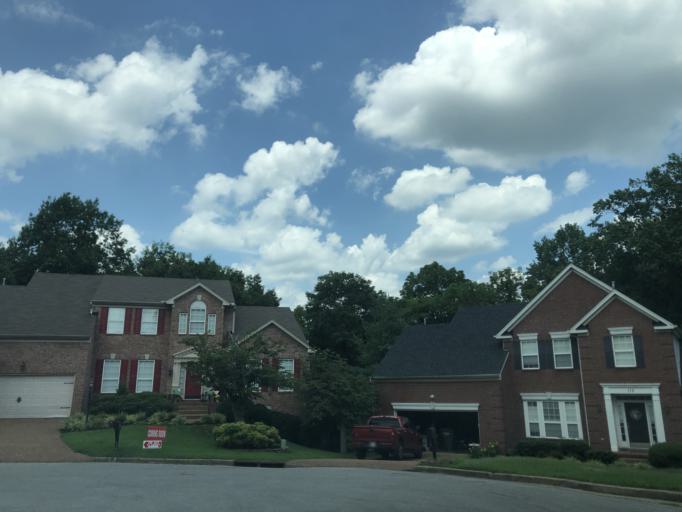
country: US
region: Tennessee
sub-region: Williamson County
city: Brentwood Estates
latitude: 36.0118
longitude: -86.7229
